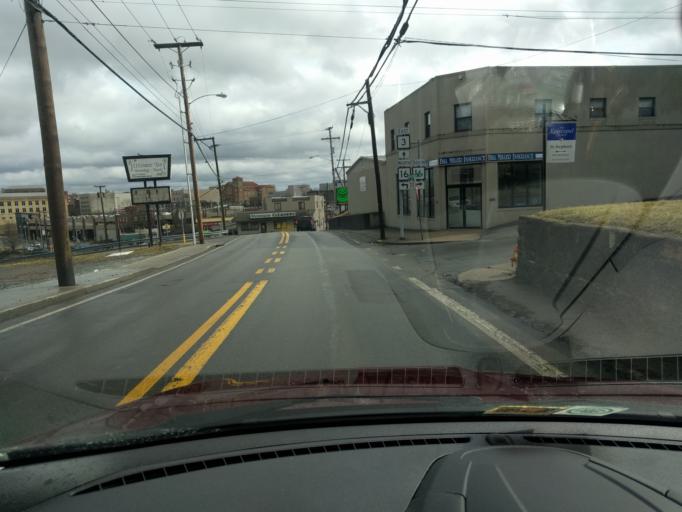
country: US
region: West Virginia
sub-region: Raleigh County
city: Beckley
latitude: 37.7762
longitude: -81.1965
